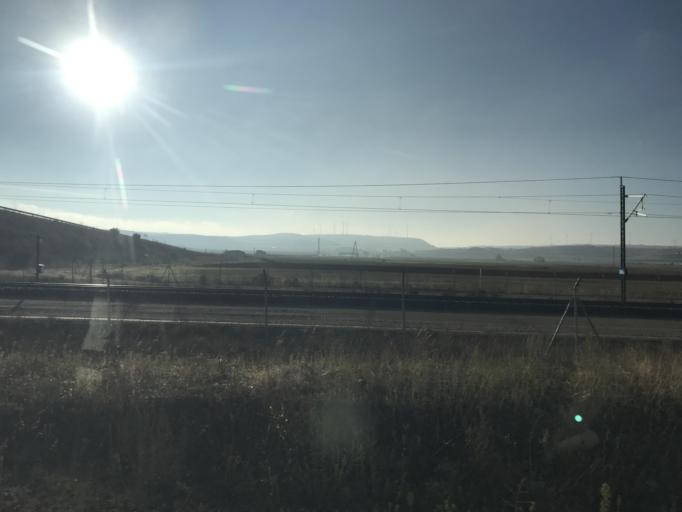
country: ES
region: Castille and Leon
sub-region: Provincia de Palencia
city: Quintana del Puente
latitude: 42.0653
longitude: -4.2214
